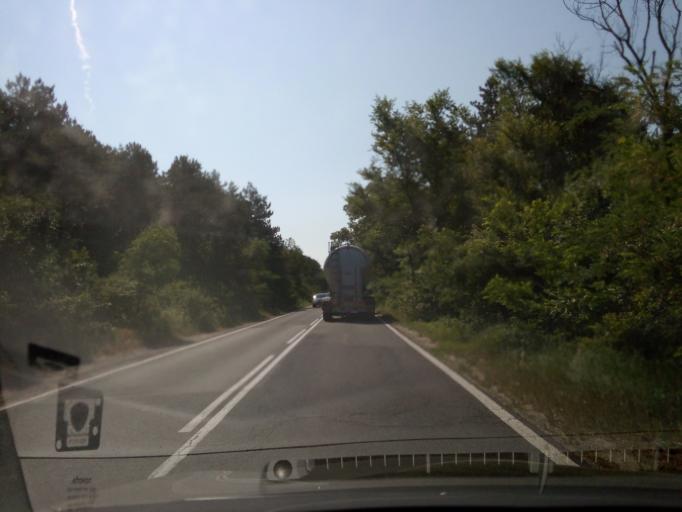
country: BG
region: Burgas
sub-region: Obshtina Nesebur
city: Sveti Vlas
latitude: 42.7717
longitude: 27.7793
